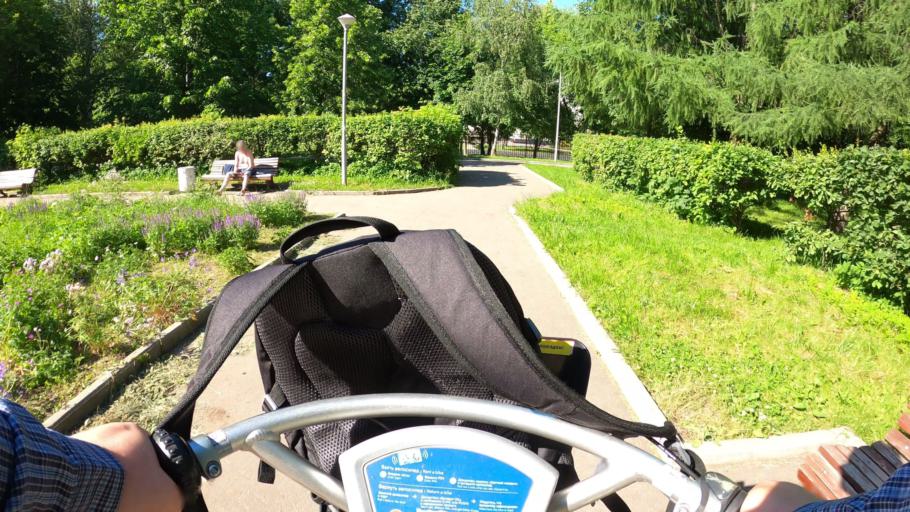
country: RU
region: Moscow
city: Chertanovo Yuzhnoye
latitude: 55.6175
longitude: 37.5968
